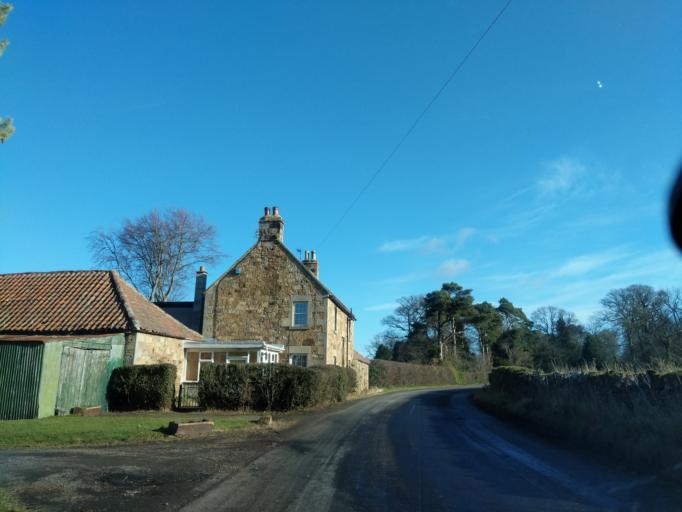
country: GB
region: Scotland
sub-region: East Lothian
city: Haddington
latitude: 55.9576
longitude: -2.7419
